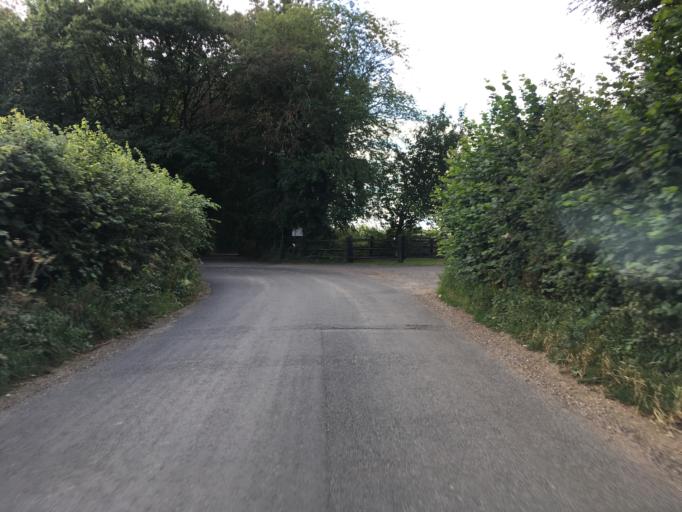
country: GB
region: England
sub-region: Kent
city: Maidstone
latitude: 51.2275
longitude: 0.5424
